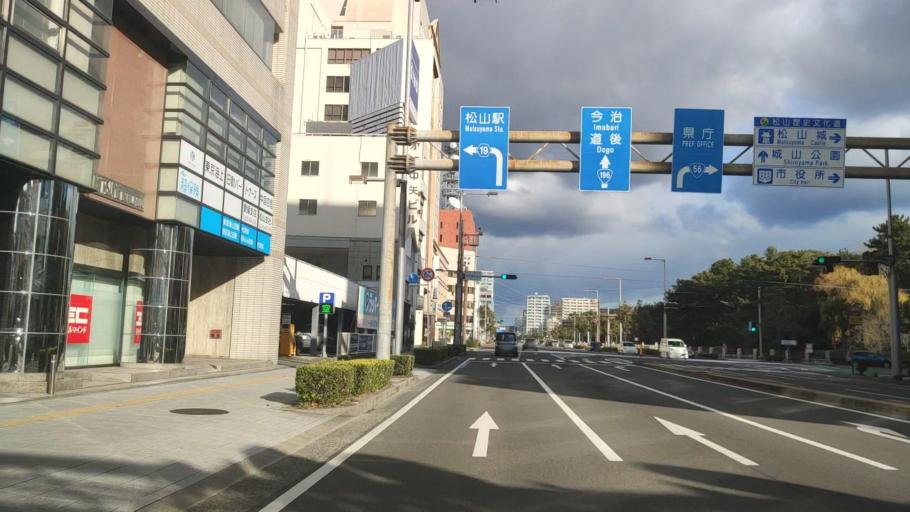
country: JP
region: Ehime
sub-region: Shikoku-chuo Shi
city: Matsuyama
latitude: 33.8389
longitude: 132.7586
